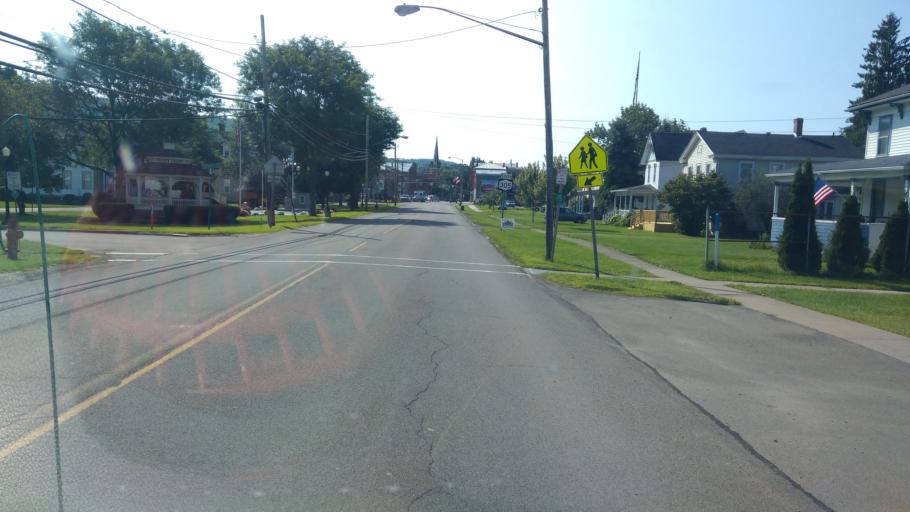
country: US
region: New York
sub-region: Allegany County
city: Cuba
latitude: 42.2193
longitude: -78.2768
